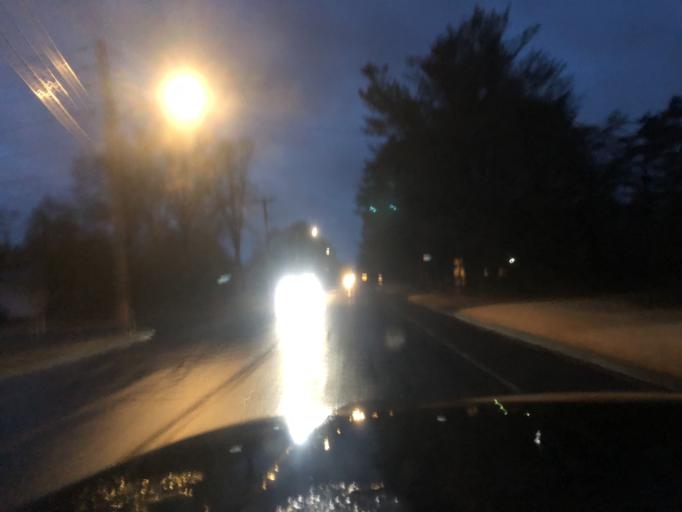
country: US
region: Connecticut
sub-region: Hartford County
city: Newington
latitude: 41.6835
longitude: -72.7431
